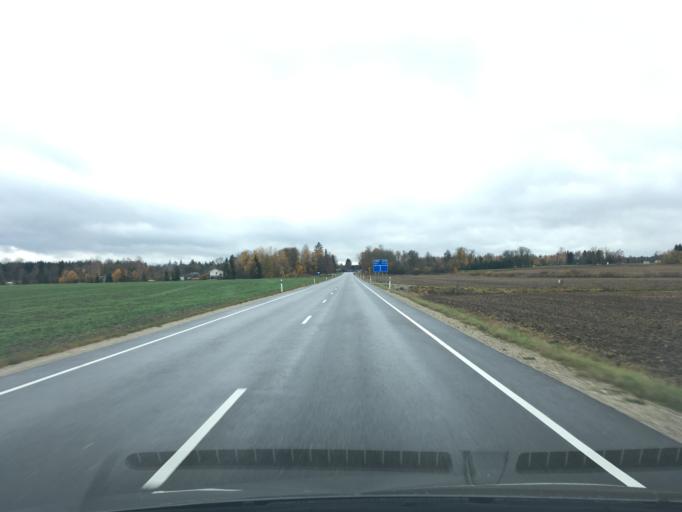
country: EE
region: Jogevamaa
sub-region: Tabivere vald
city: Tabivere
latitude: 58.4342
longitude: 26.4909
